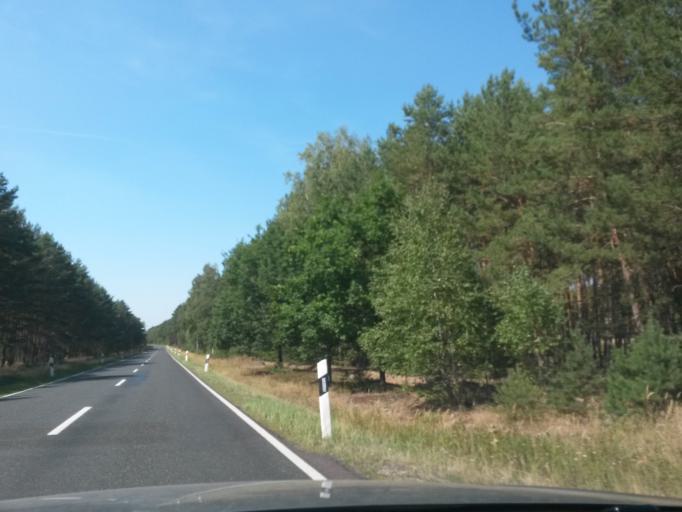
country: DE
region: Brandenburg
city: Wiesenburg
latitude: 52.1694
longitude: 12.4316
